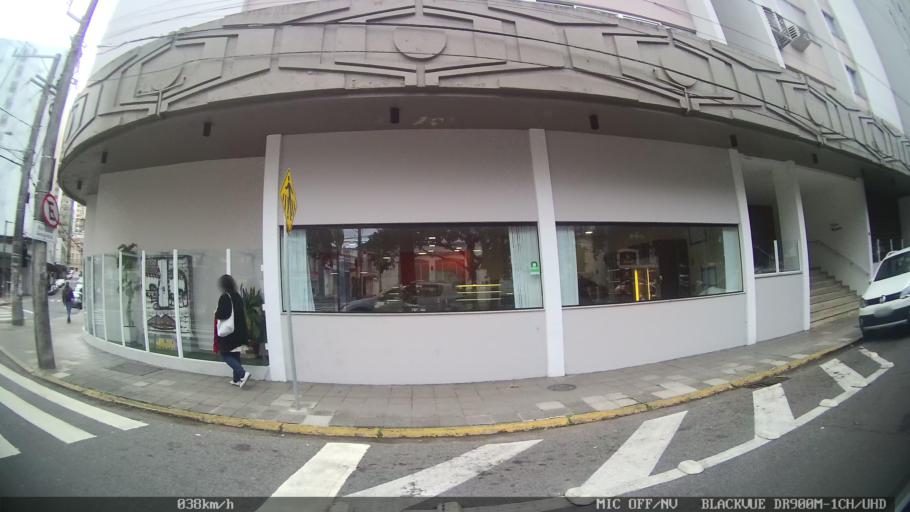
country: BR
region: Santa Catarina
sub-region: Florianopolis
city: Florianopolis
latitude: -27.5967
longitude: -48.5468
